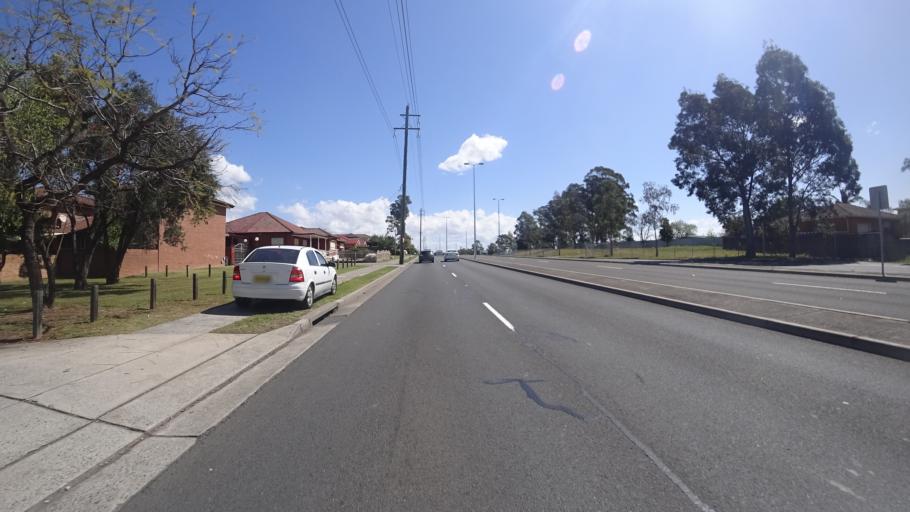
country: AU
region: New South Wales
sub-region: Liverpool
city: Miller
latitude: -33.9274
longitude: 150.9059
